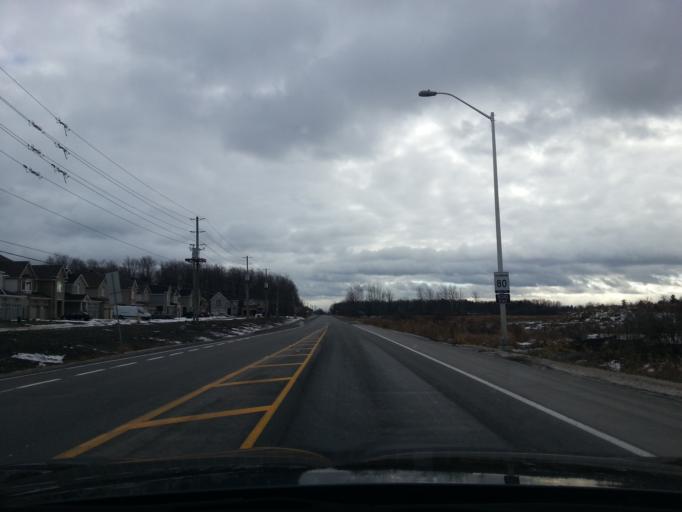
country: CA
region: Ontario
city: Bells Corners
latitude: 45.2413
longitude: -75.7290
